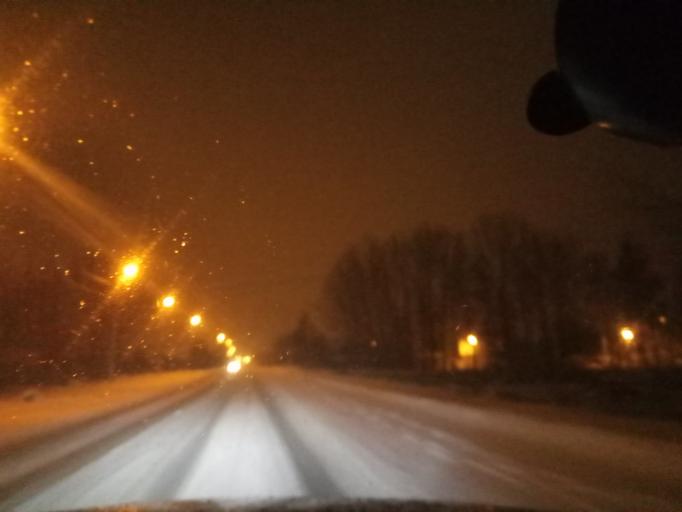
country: RU
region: Tula
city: Novomoskovsk
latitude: 53.9949
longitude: 38.2945
